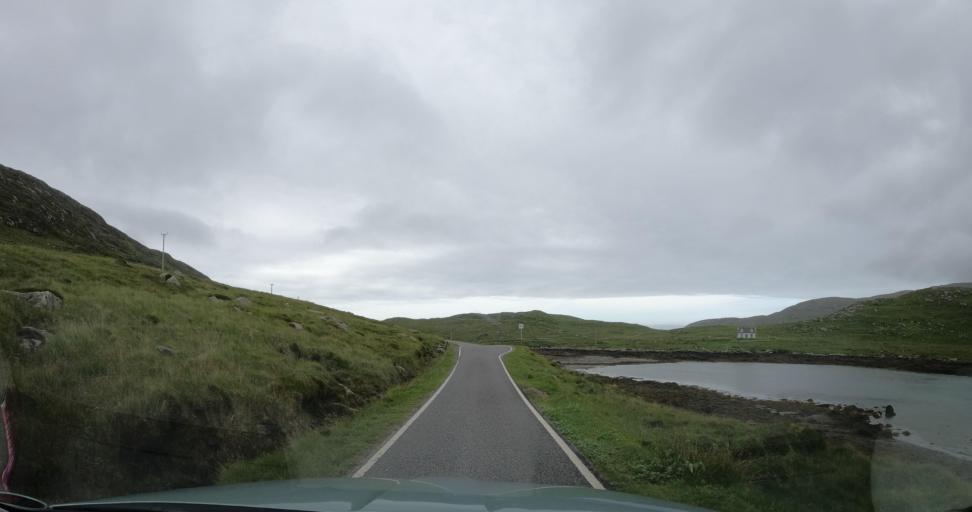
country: GB
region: Scotland
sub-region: Eilean Siar
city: Barra
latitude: 56.9384
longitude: -7.5386
